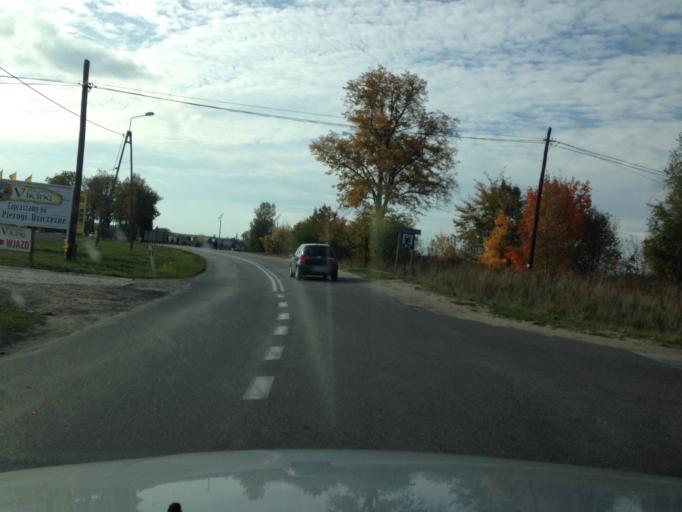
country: PL
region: Pomeranian Voivodeship
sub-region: Powiat koscierski
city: Stara Kiszewa
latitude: 53.9925
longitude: 18.1808
